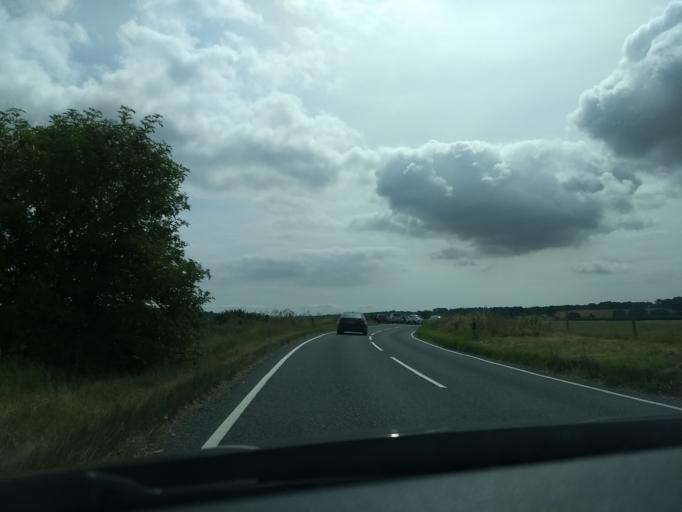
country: GB
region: England
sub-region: Suffolk
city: Ipswich
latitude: 52.0258
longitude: 1.1602
